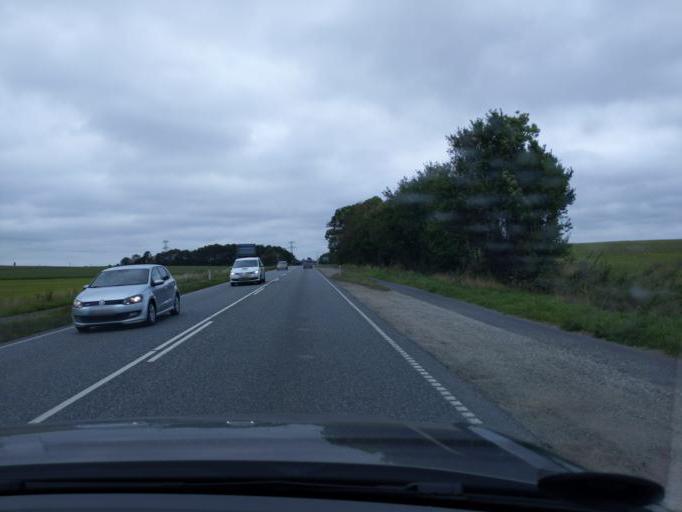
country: DK
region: Central Jutland
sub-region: Randers Kommune
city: Randers
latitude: 56.4878
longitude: 9.9864
